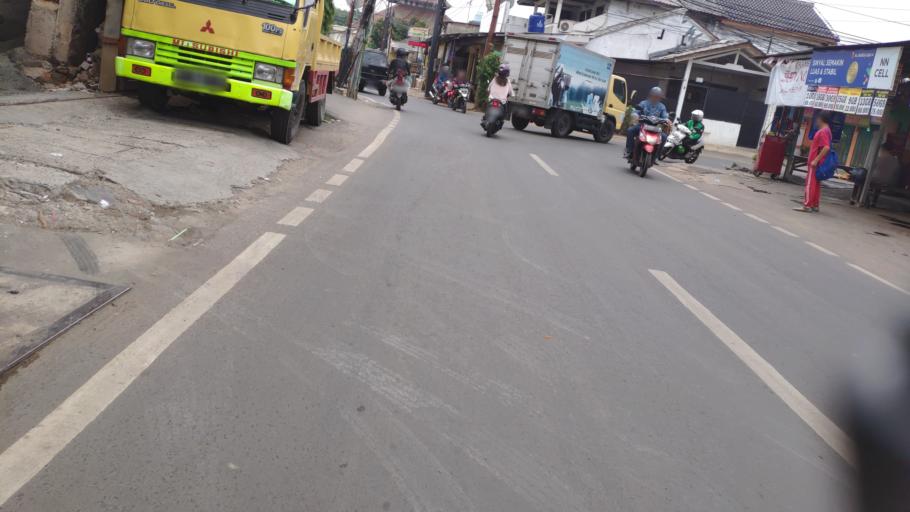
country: ID
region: West Java
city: Depok
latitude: -6.3460
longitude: 106.8260
